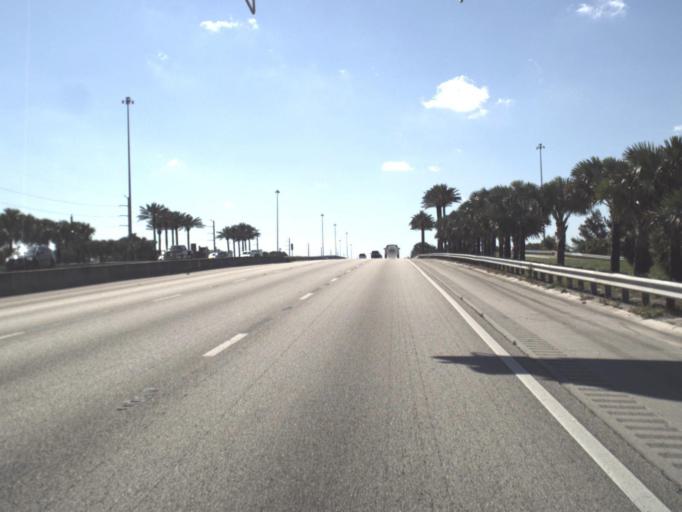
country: US
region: Florida
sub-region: Miami-Dade County
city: Doral
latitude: 25.8138
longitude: -80.3866
